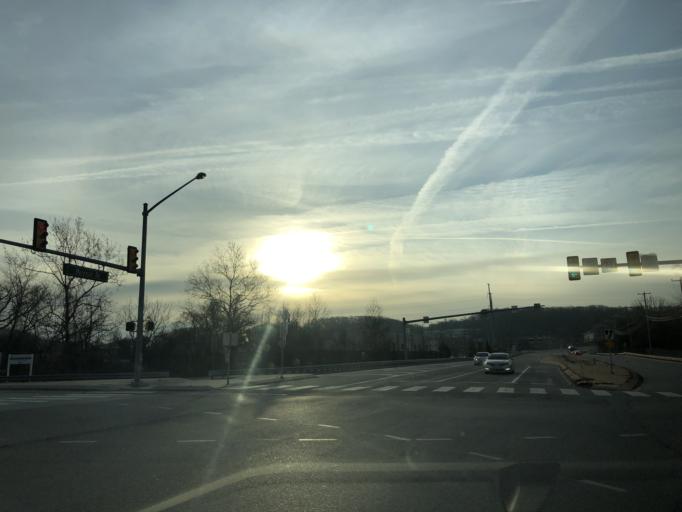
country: US
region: Pennsylvania
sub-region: Chester County
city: Malvern
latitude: 40.0498
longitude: -75.5252
